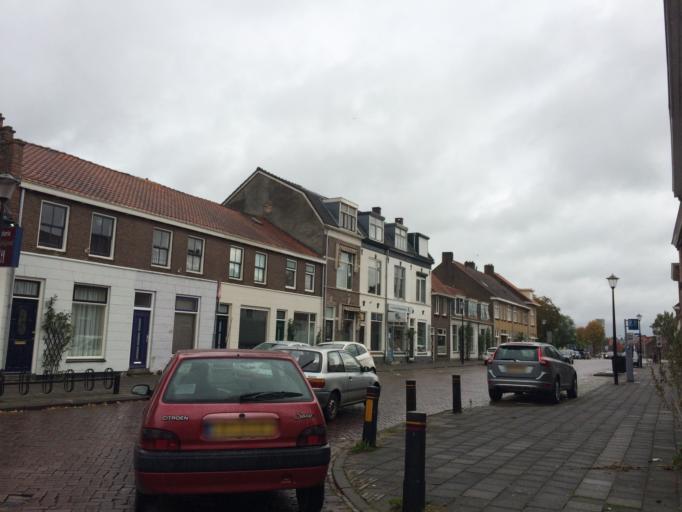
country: NL
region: Gelderland
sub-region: Gemeente Culemborg
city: Culemborg
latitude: 51.9536
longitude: 5.2284
